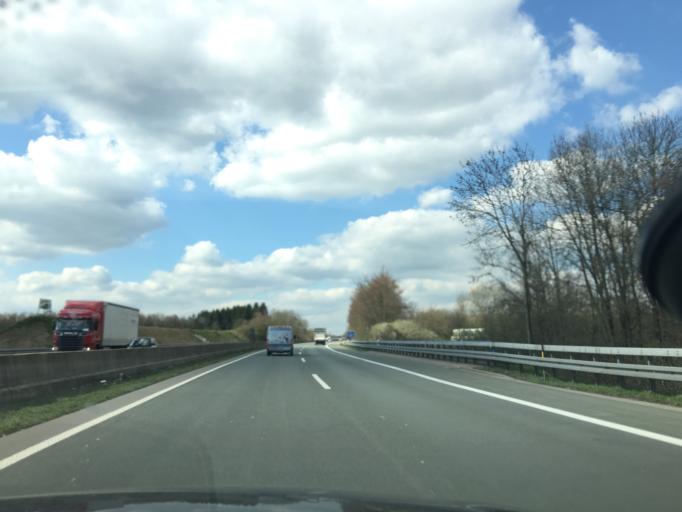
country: DE
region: North Rhine-Westphalia
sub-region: Regierungsbezirk Arnsberg
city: Wenden
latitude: 50.9553
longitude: 7.8506
